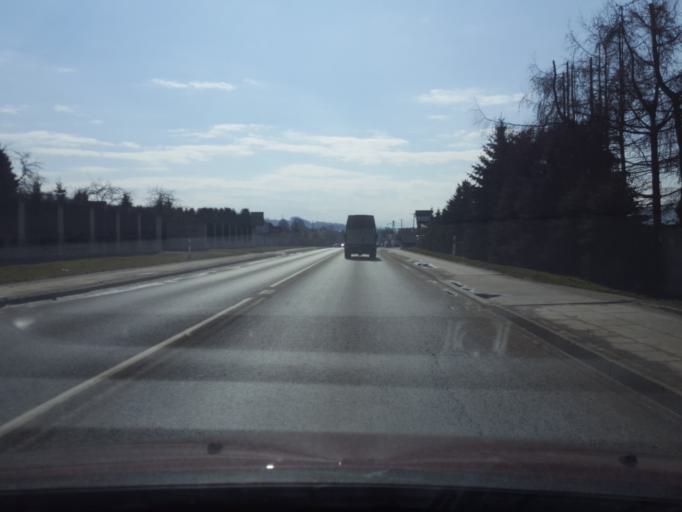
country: PL
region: Lesser Poland Voivodeship
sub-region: Powiat nowosadecki
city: Chelmiec
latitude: 49.6747
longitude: 20.6831
